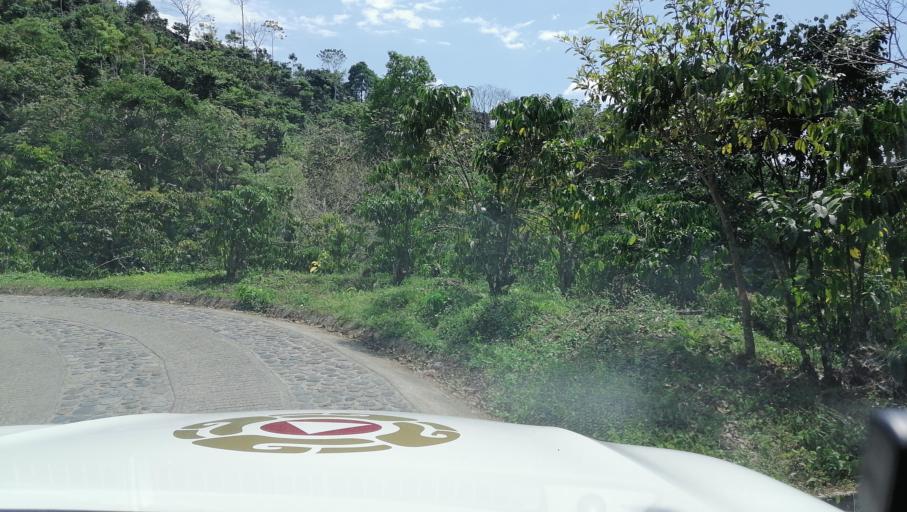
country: MX
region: Chiapas
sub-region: Tapachula
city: Canton Villaflor
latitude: 15.1379
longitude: -92.2886
